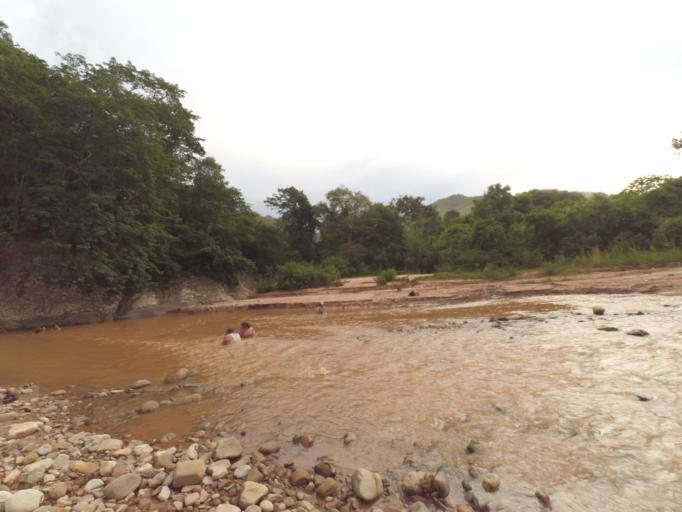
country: BO
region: Chuquisaca
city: Monteagudo
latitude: -19.8030
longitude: -64.0111
